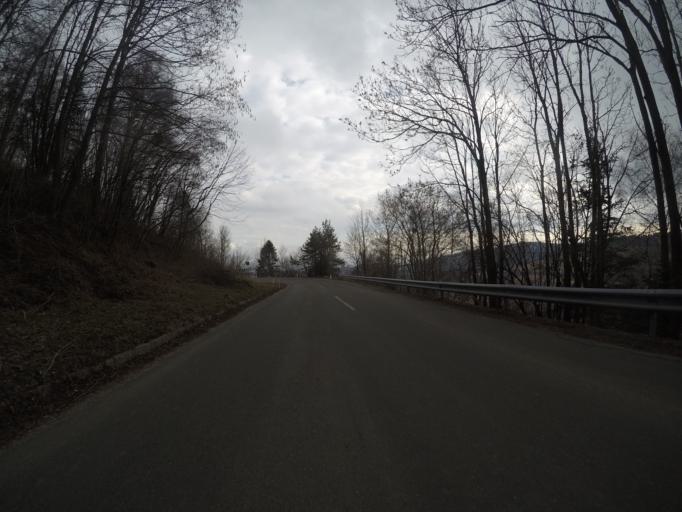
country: SI
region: Ruse
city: Bistrica ob Dravi
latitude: 46.4945
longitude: 15.5631
